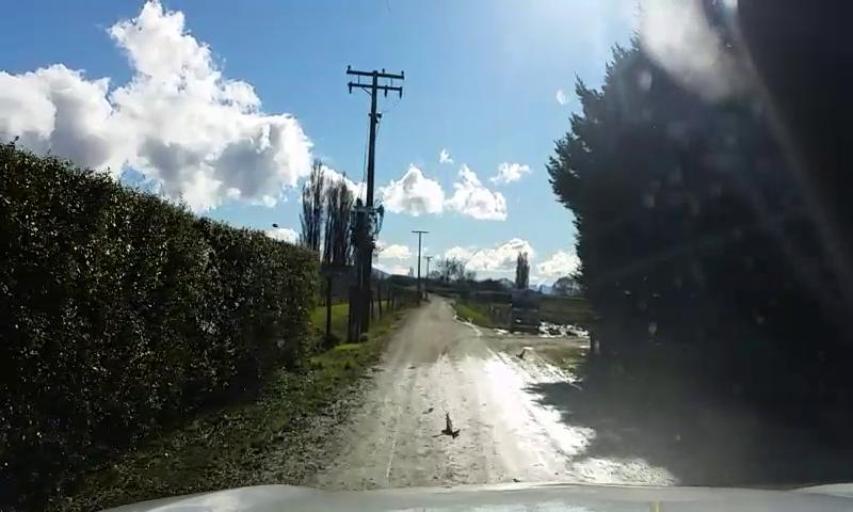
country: NZ
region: Tasman
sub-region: Tasman District
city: Richmond
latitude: -41.3007
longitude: 173.1420
